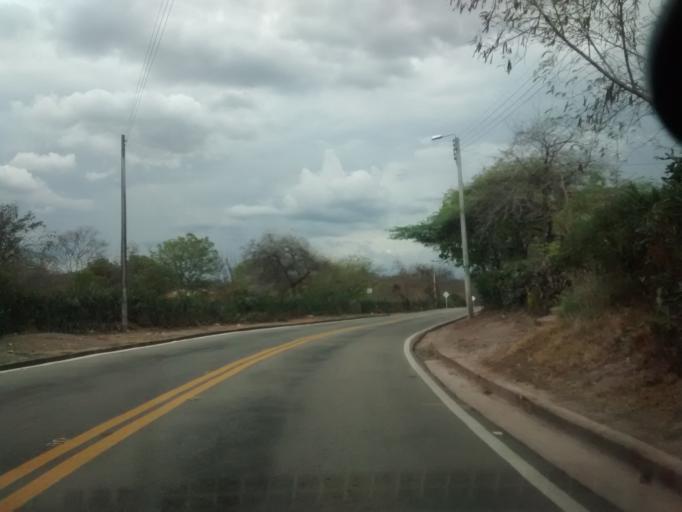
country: CO
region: Cundinamarca
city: Agua de Dios
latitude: 4.4280
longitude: -74.6958
